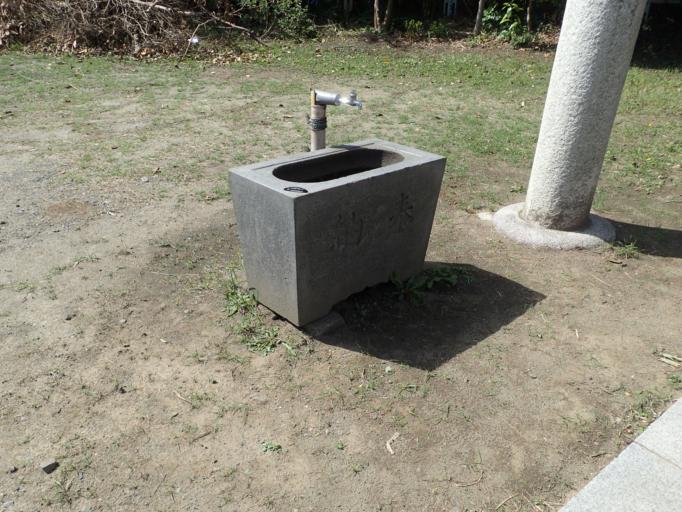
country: JP
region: Kanagawa
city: Zushi
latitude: 35.3617
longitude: 139.6063
